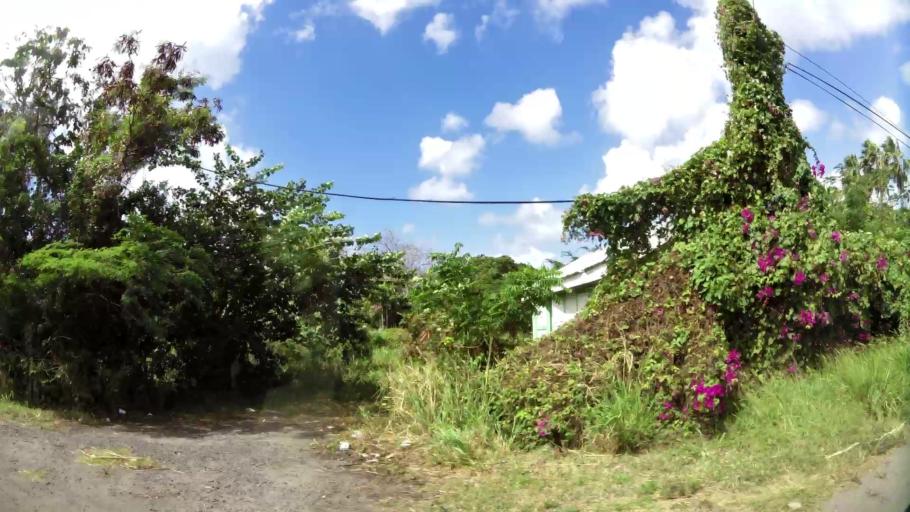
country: KN
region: Saint Thomas Lowland
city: Cotton Ground
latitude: 17.1802
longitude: -62.6218
